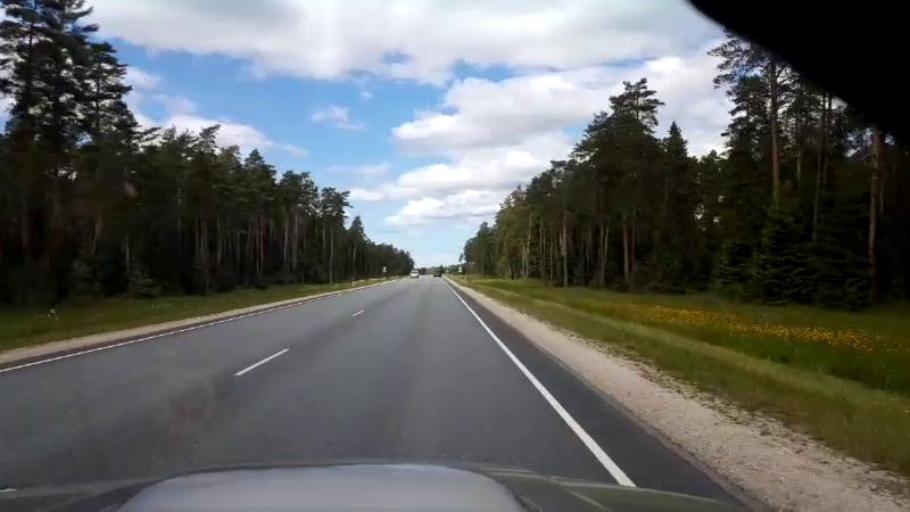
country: EE
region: Raplamaa
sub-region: Maerjamaa vald
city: Marjamaa
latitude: 59.0189
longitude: 24.4518
